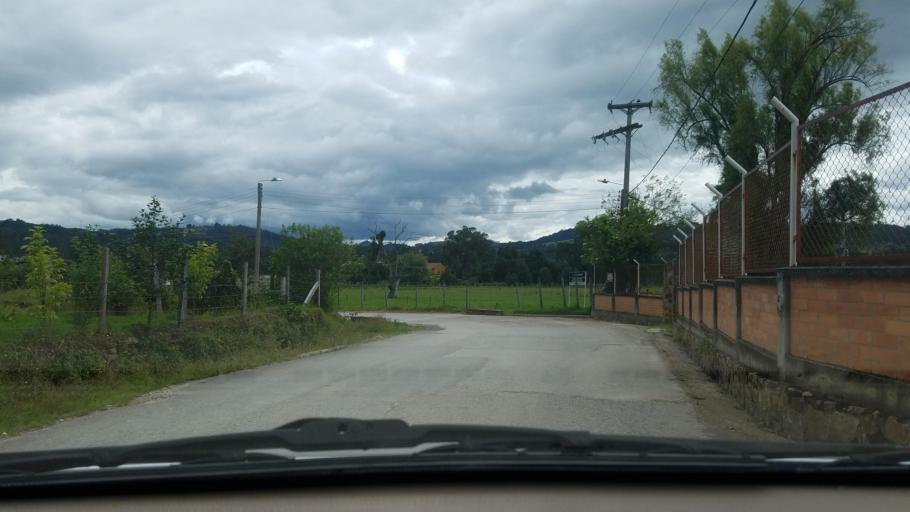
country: CO
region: Boyaca
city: Paipa
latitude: 5.7501
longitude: -73.1071
